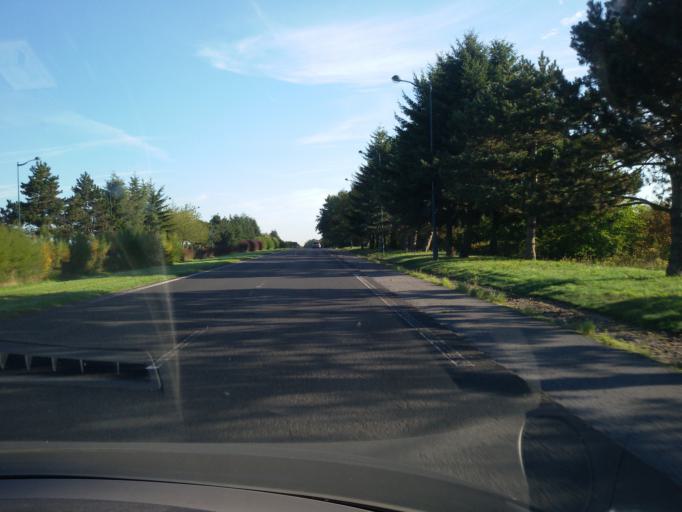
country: FR
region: Ile-de-France
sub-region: Departement de Seine-et-Marne
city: Serris
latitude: 48.8636
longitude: 2.7950
